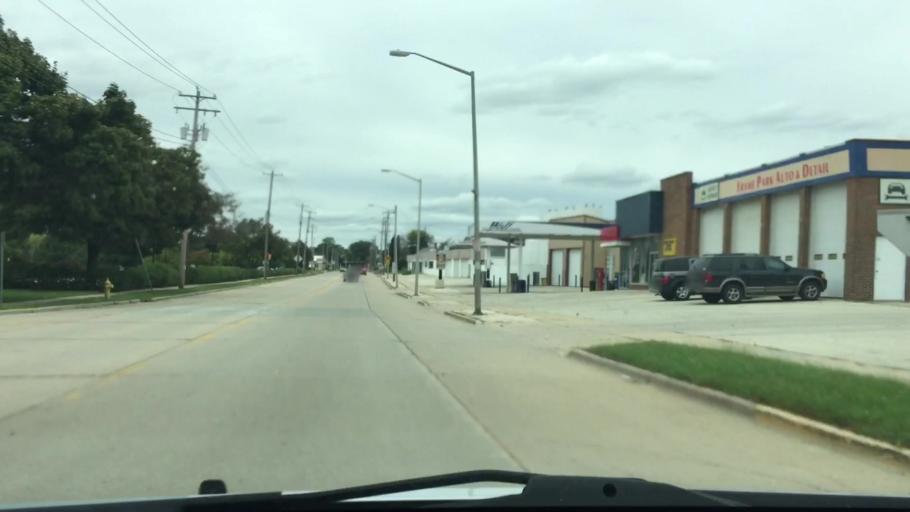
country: US
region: Wisconsin
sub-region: Waukesha County
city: Waukesha
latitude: 43.0173
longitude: -88.2224
